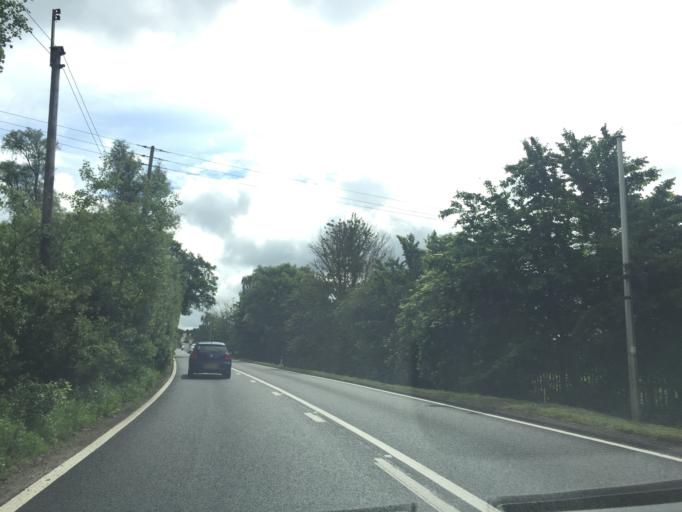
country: GB
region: England
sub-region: Dorset
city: Lytchett Matravers
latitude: 50.7861
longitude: -2.0422
